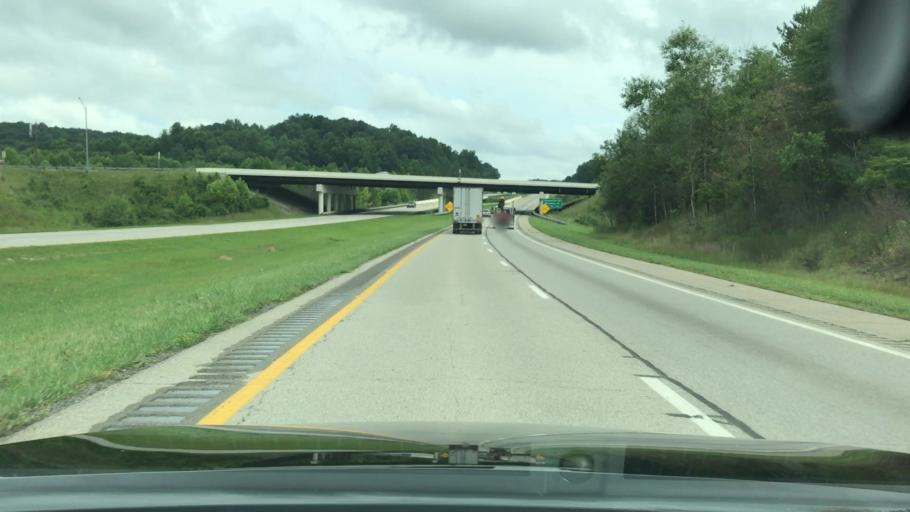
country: US
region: Ohio
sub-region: Jackson County
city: Jackson
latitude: 39.0740
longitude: -82.6295
